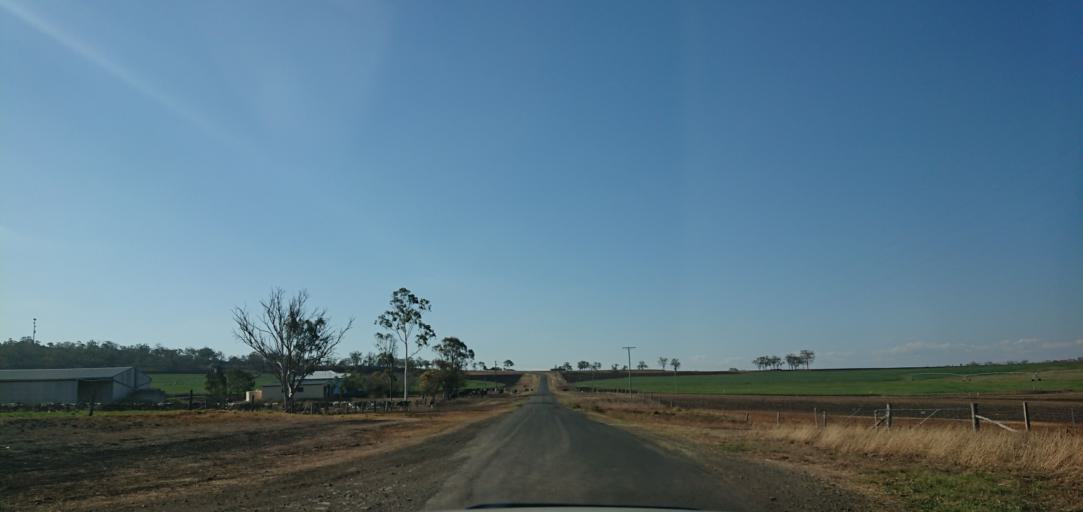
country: AU
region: Queensland
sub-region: Toowoomba
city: Westbrook
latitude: -27.7084
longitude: 151.7162
